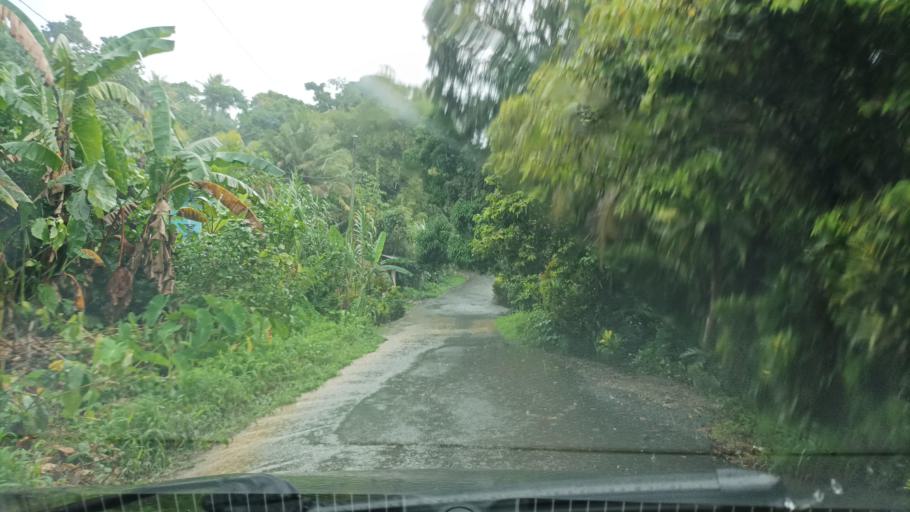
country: FM
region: Pohnpei
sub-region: Kolonia Municipality
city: Kolonia
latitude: 6.9605
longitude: 158.2251
